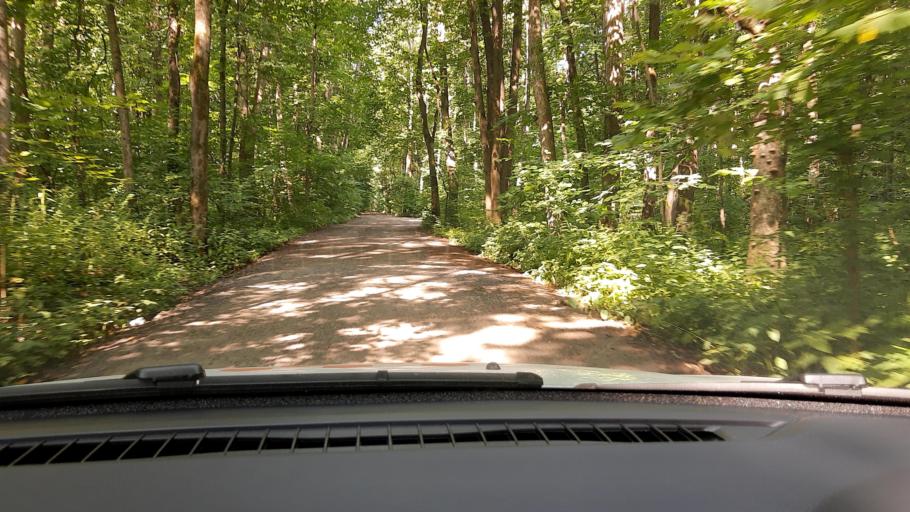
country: RU
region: Nizjnij Novgorod
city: Burevestnik
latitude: 56.0531
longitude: 43.9934
